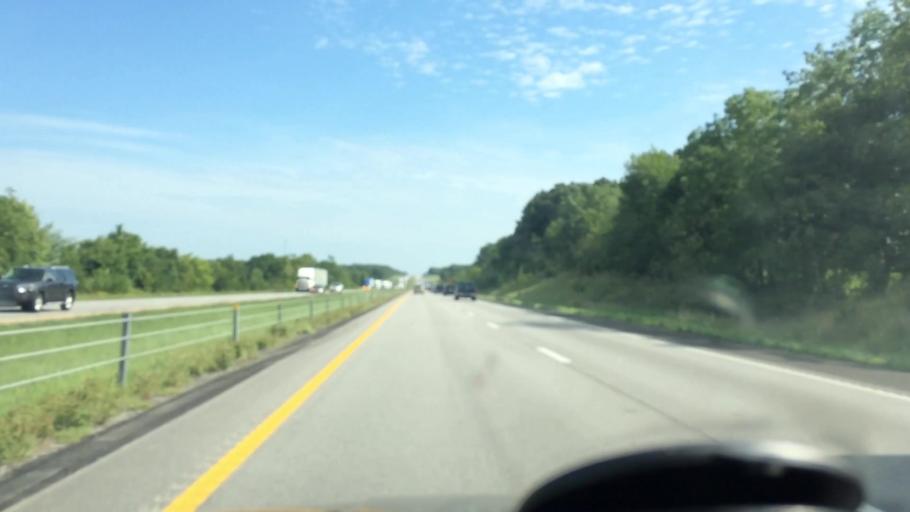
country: US
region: Missouri
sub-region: Webster County
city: Marshfield
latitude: 37.4609
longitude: -92.8637
